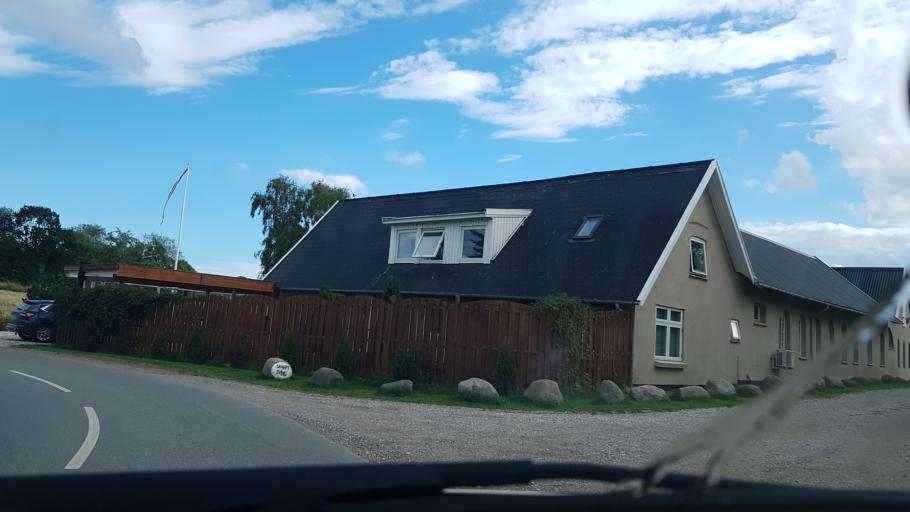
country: DK
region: Capital Region
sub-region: Fredensborg Kommune
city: Niva
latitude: 55.9520
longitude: 12.5072
